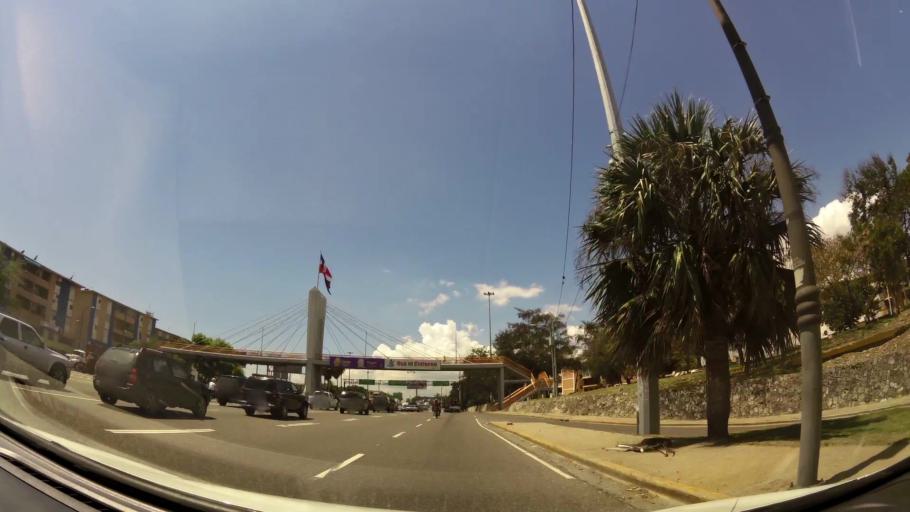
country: DO
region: Nacional
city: San Carlos
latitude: 18.4869
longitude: -69.8861
